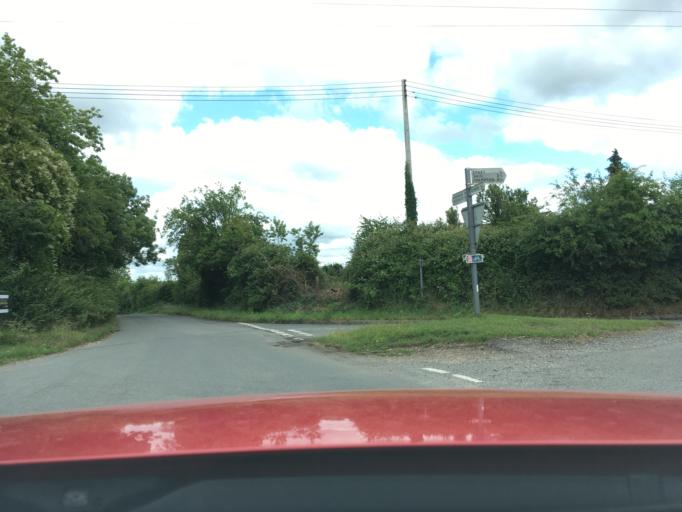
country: GB
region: England
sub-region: Gloucestershire
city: Stonehouse
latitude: 51.8088
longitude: -2.3432
